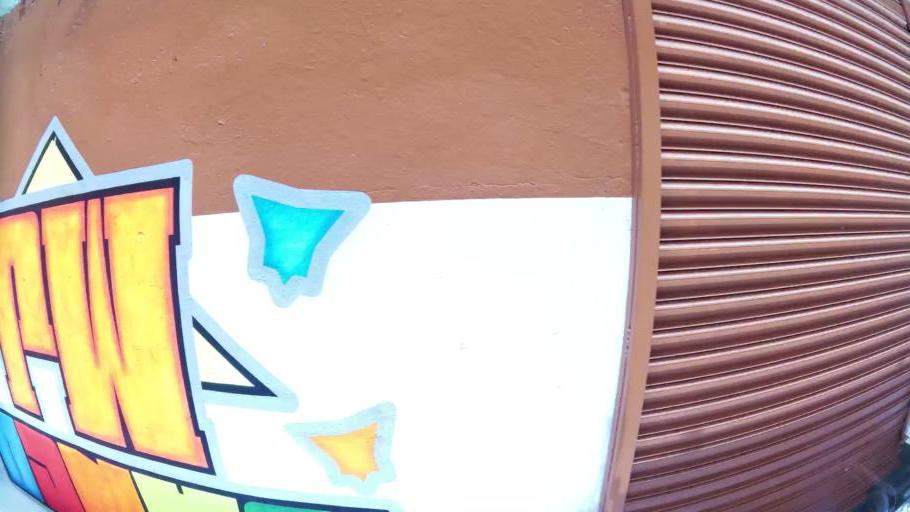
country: DO
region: Nacional
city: La Agustina
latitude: 18.5226
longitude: -69.9170
